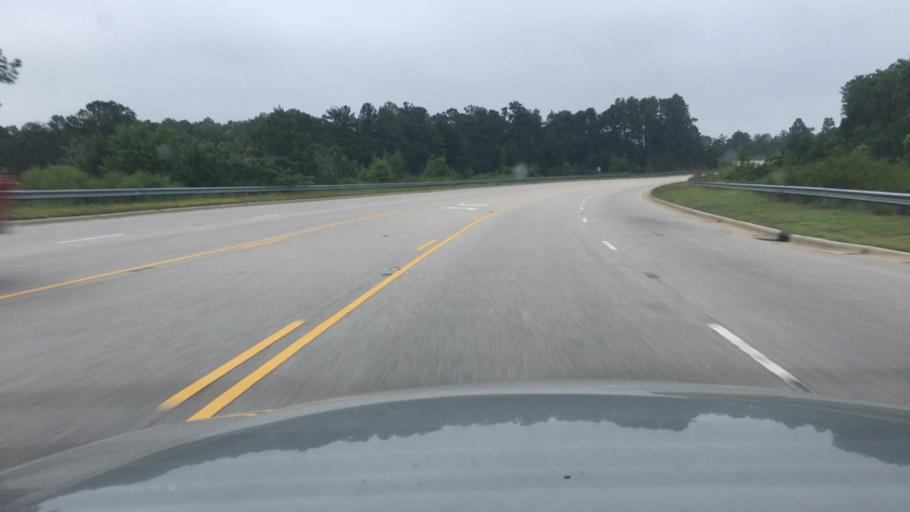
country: US
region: North Carolina
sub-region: Cumberland County
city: Fayetteville
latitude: 35.0162
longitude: -78.8896
